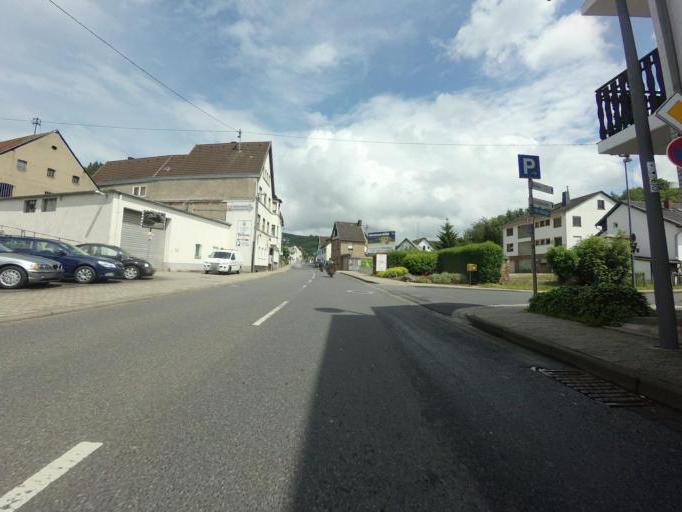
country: DE
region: Rheinland-Pfalz
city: Adenau
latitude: 50.3817
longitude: 6.9356
